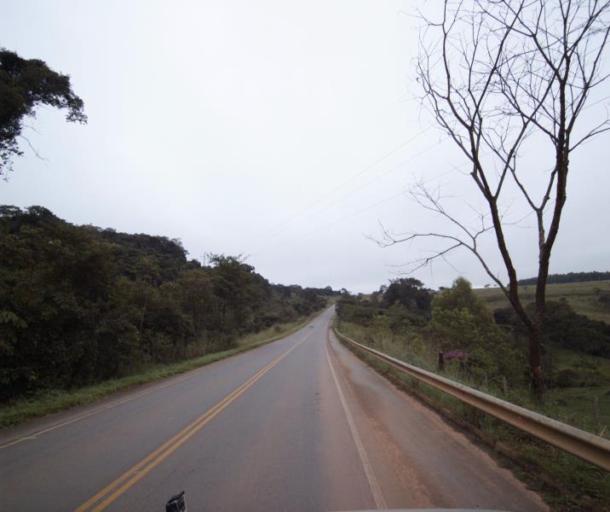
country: BR
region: Goias
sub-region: Pirenopolis
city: Pirenopolis
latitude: -15.9603
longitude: -48.8164
